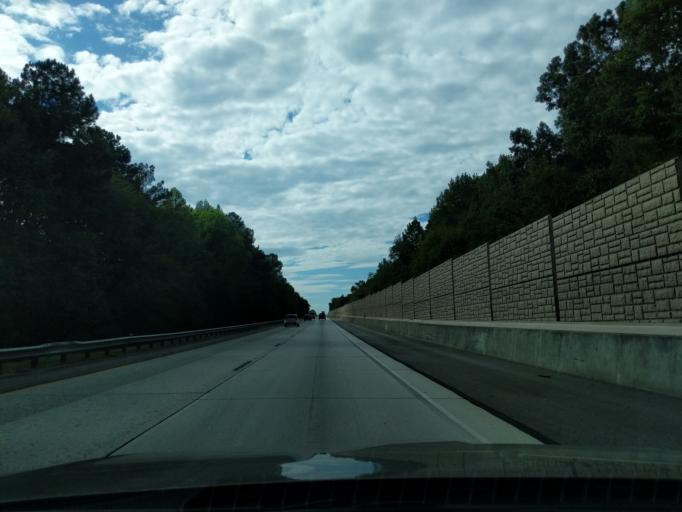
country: US
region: Georgia
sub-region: Columbia County
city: Grovetown
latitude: 33.4793
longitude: -82.1535
